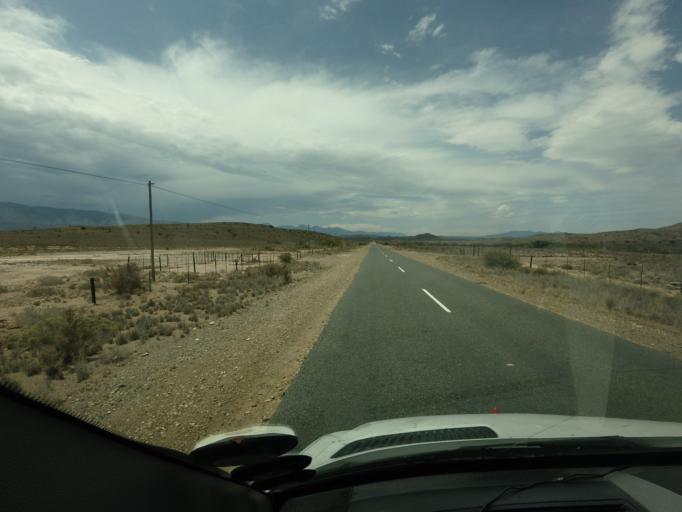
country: ZA
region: Western Cape
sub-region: Eden District Municipality
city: Ladismith
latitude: -33.6651
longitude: 20.9984
